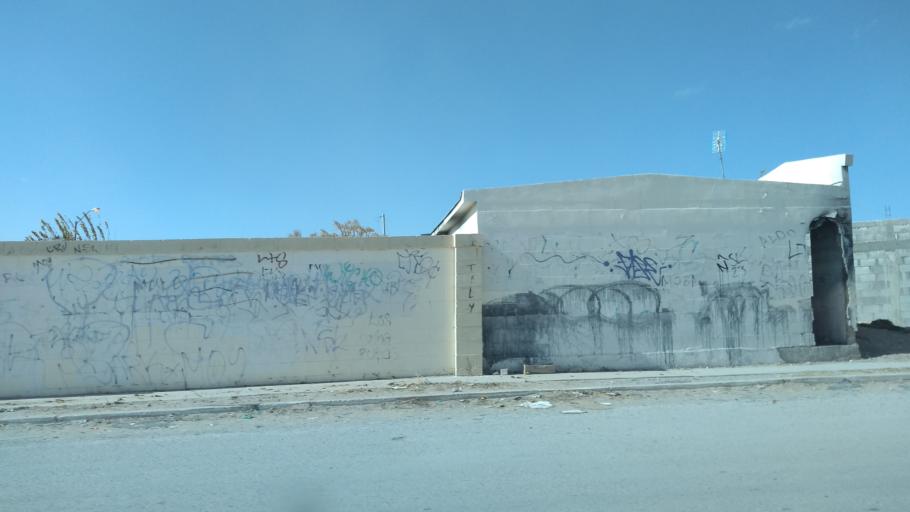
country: US
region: Texas
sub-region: El Paso County
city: San Elizario
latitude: 31.5693
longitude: -106.3317
